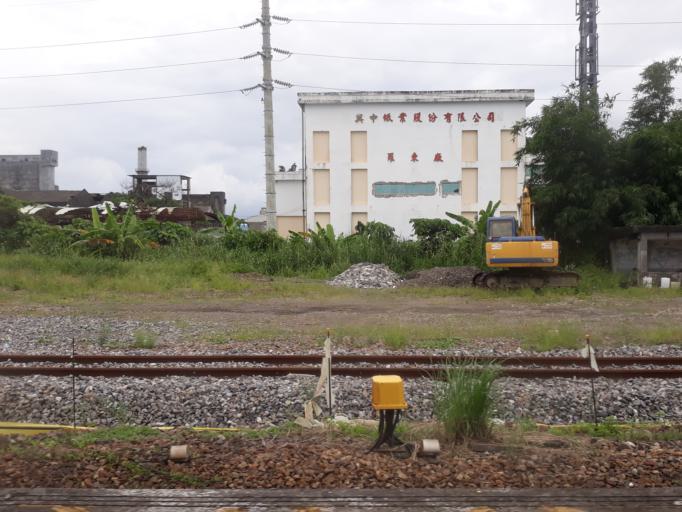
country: TW
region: Taiwan
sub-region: Yilan
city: Yilan
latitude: 24.6955
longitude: 121.7752
